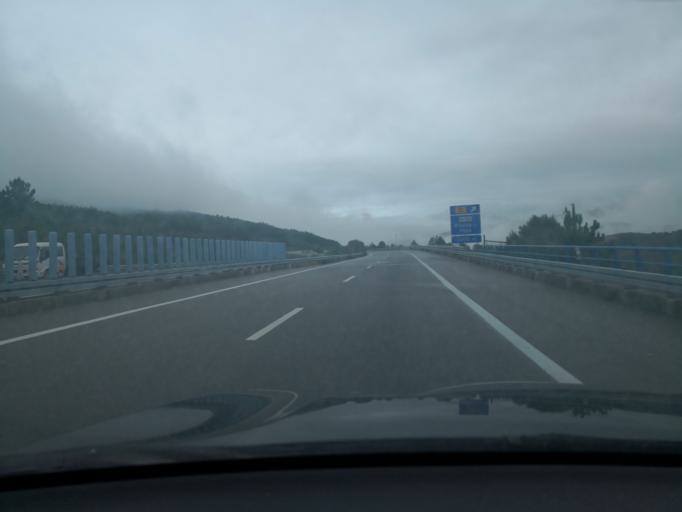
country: PT
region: Vila Real
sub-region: Ribeira de Pena
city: Ribeira de Pena
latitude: 41.4939
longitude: -7.8256
